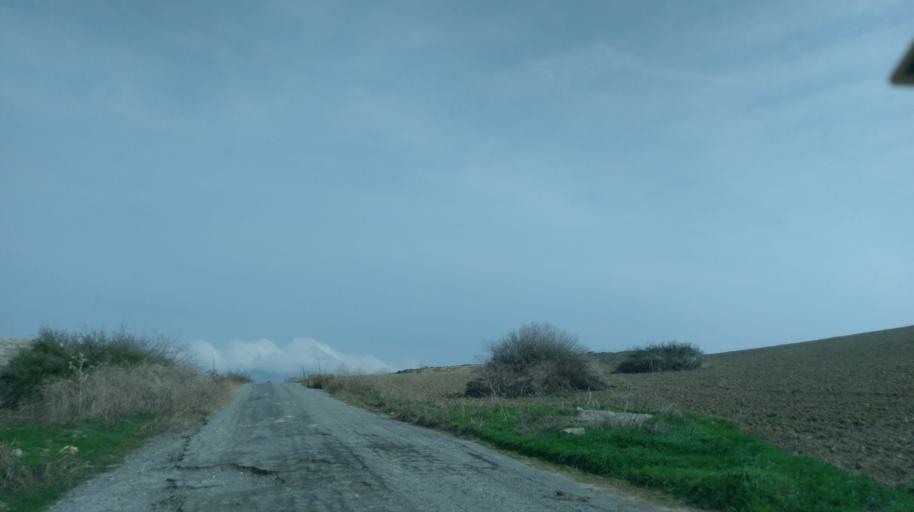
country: CY
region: Lefkosia
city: Morfou
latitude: 35.2522
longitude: 33.0767
